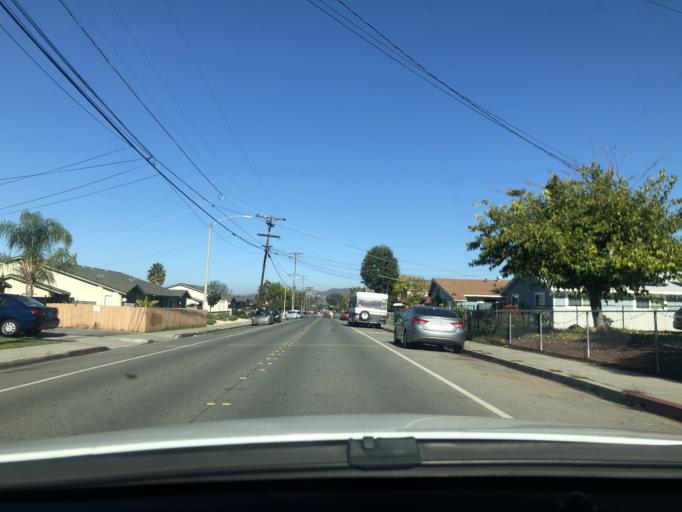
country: US
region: California
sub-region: San Diego County
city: El Cajon
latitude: 32.7851
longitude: -116.9483
